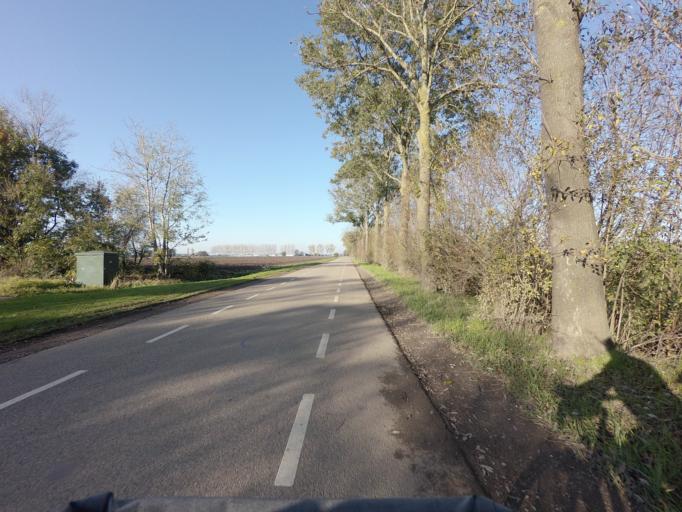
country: NL
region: North Brabant
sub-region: Gemeente Woudrichem
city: Woudrichem
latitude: 51.7627
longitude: 5.0511
